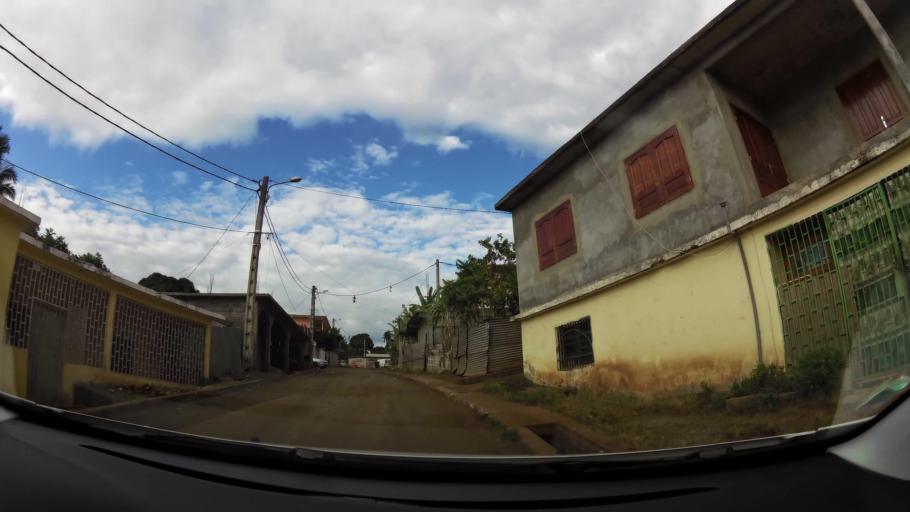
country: YT
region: Ouangani
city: Ouangani
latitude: -12.8386
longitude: 45.1591
